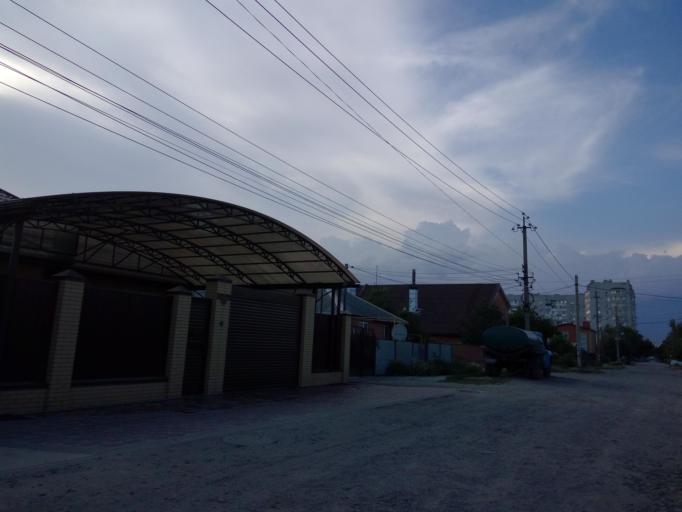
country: RU
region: Rostov
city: Bataysk
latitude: 47.1193
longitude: 39.7358
